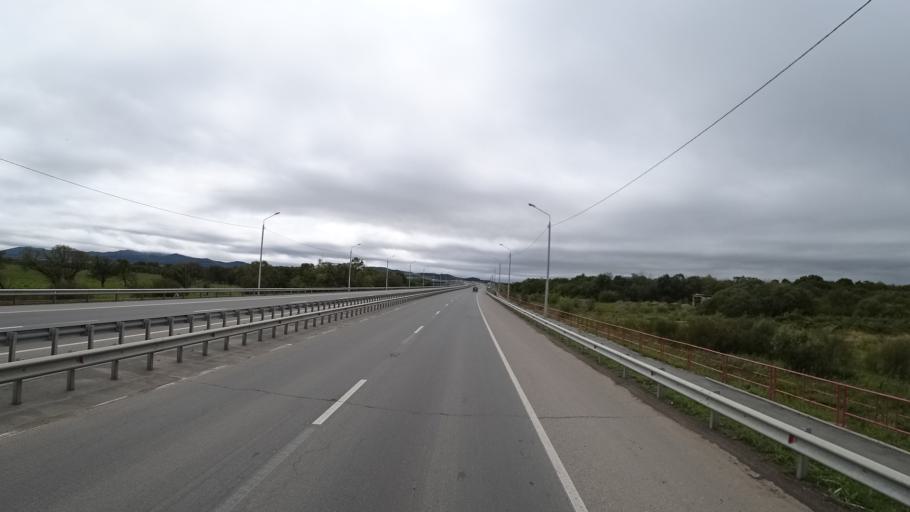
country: RU
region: Primorskiy
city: Monastyrishche
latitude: 44.1988
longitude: 132.4474
